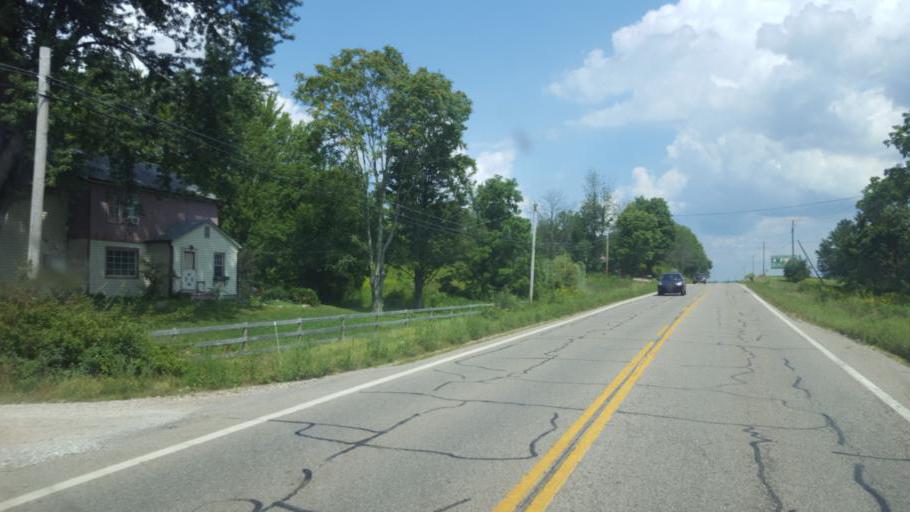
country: US
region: Ohio
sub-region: Knox County
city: Mount Vernon
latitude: 40.3535
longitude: -82.5493
